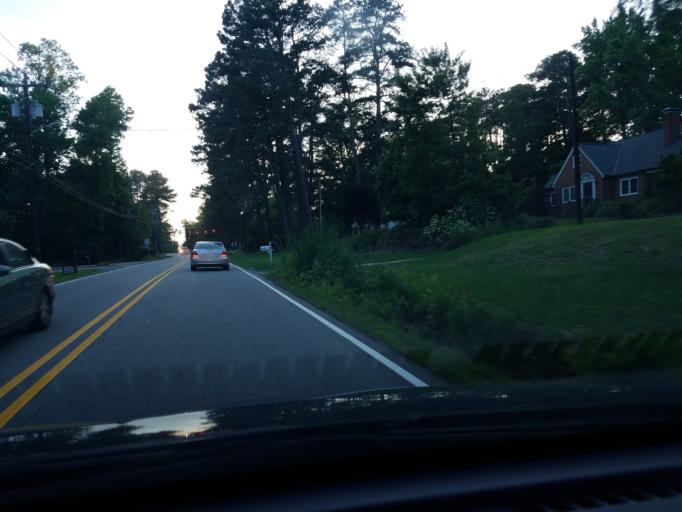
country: US
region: North Carolina
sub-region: Durham County
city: Durham
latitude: 35.9706
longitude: -78.9307
